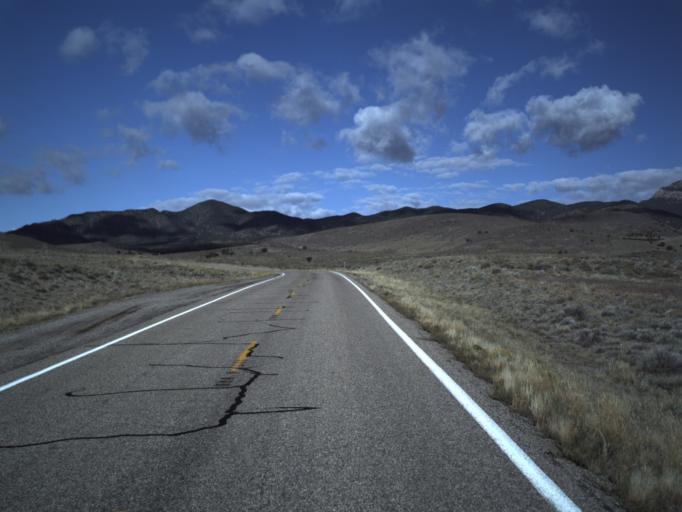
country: US
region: Utah
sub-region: Beaver County
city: Milford
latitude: 38.4563
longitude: -113.2180
